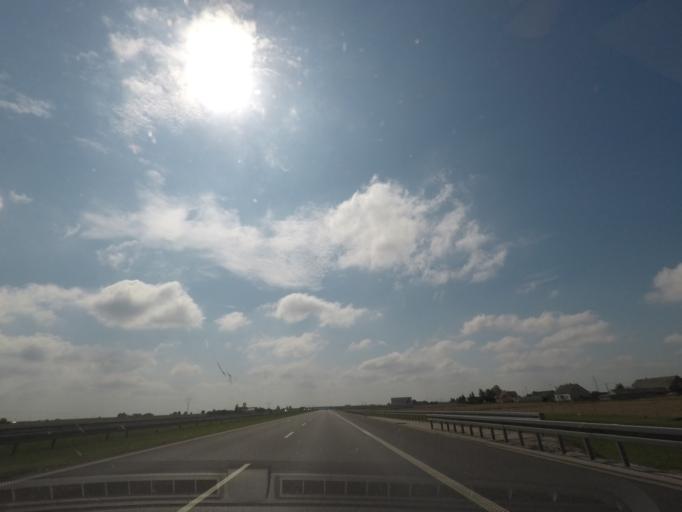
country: PL
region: Kujawsko-Pomorskie
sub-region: Powiat wloclawski
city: Lubanie
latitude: 52.7216
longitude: 18.8680
